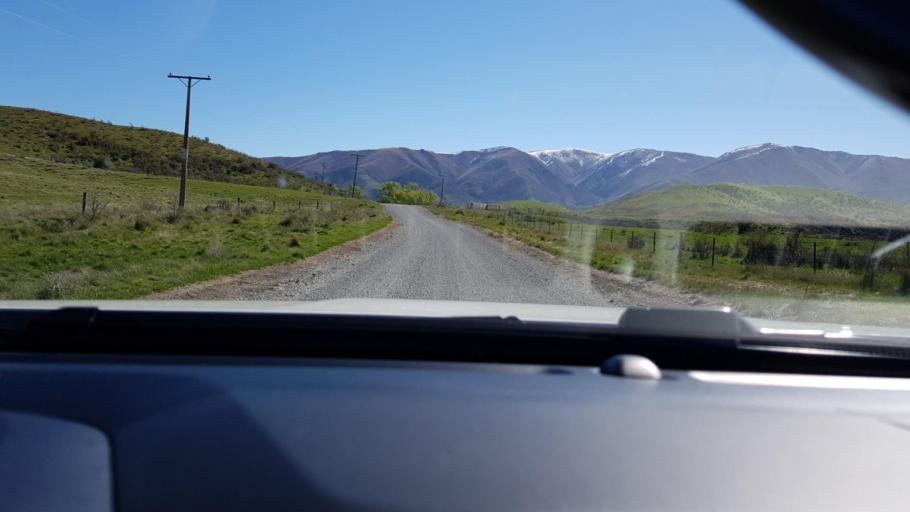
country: NZ
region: Otago
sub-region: Queenstown-Lakes District
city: Wanaka
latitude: -44.4621
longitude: 169.8863
